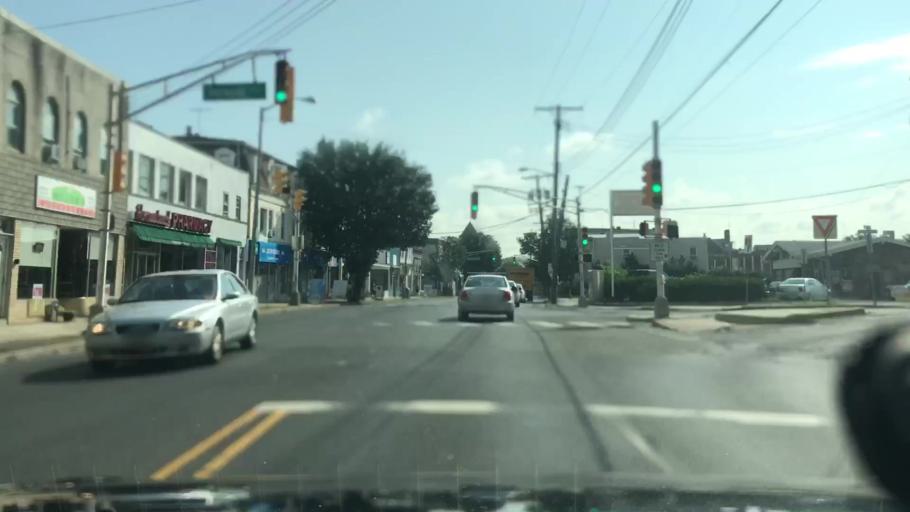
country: US
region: New Jersey
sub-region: Monmouth County
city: Long Branch
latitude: 40.2996
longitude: -74.0034
